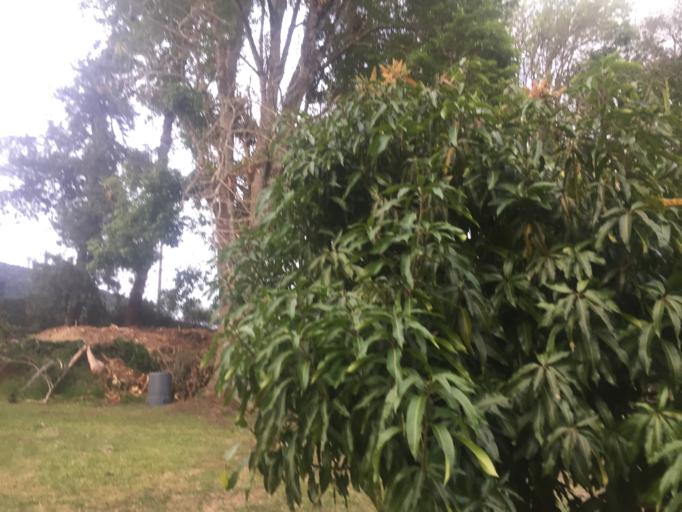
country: CO
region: Valle del Cauca
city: Calimita
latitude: 3.8811
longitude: -76.5386
